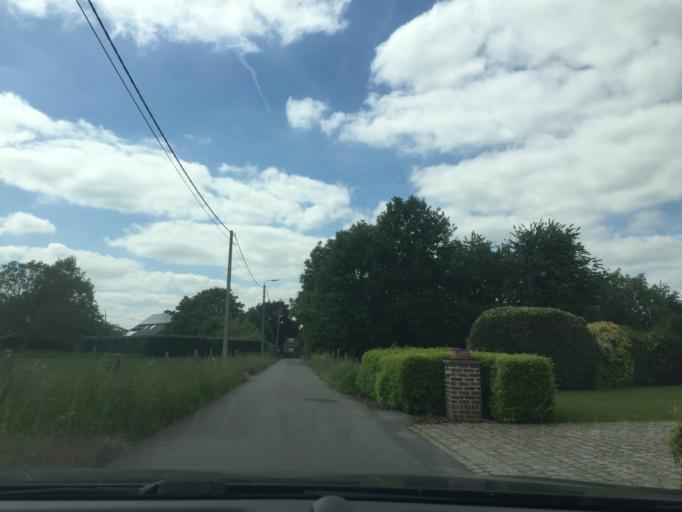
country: BE
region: Flanders
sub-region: Provincie West-Vlaanderen
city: Lendelede
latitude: 50.8618
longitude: 3.2378
